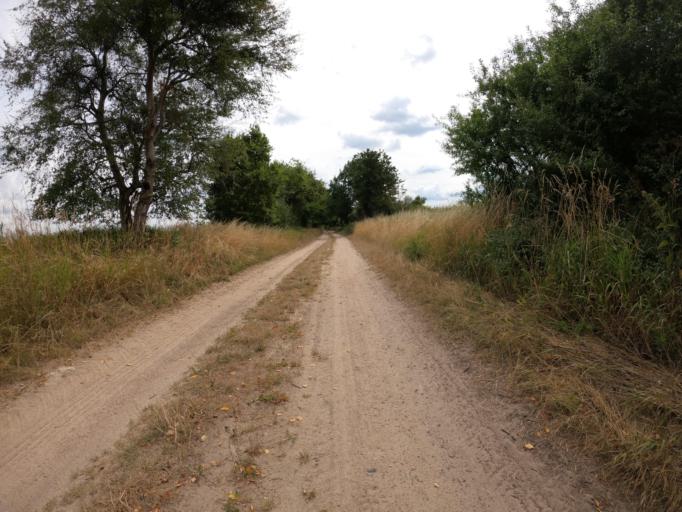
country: DE
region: Mecklenburg-Vorpommern
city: Loitz
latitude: 53.3938
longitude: 13.4433
